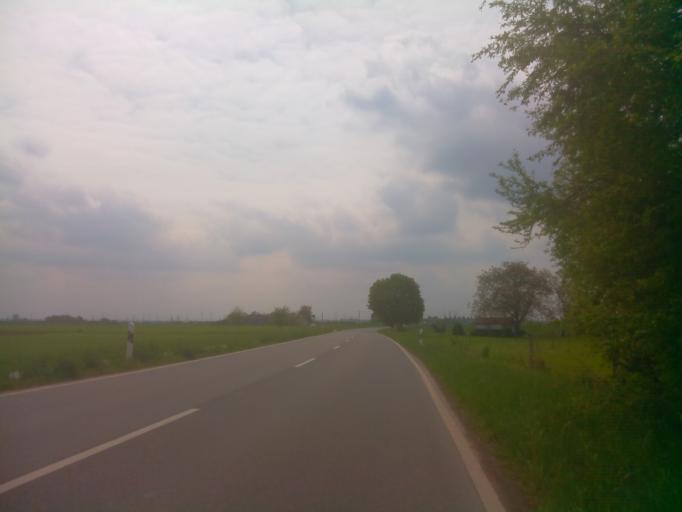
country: DE
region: Baden-Wuerttemberg
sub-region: Karlsruhe Region
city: Edingen-Neckarhausen
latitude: 49.4342
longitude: 8.6010
